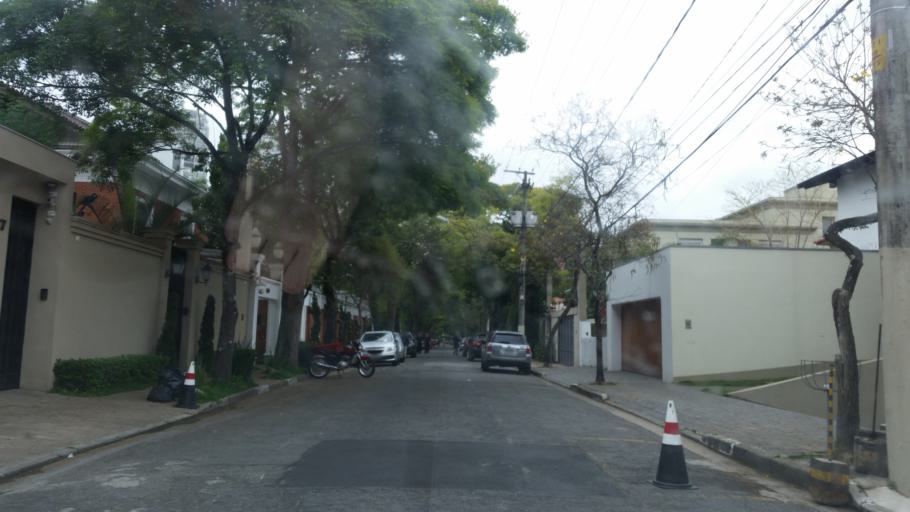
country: BR
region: Sao Paulo
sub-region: Sao Paulo
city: Sao Paulo
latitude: -23.5949
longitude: -46.6605
